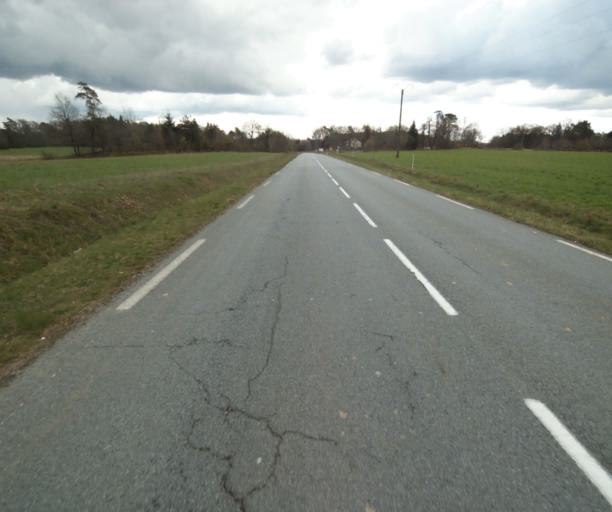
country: FR
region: Limousin
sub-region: Departement de la Correze
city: Correze
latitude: 45.2853
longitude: 1.9069
